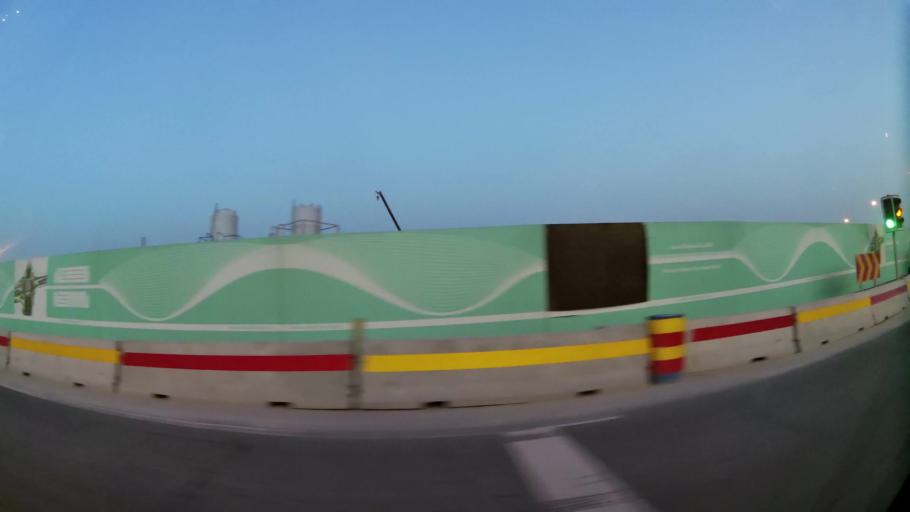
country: QA
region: Baladiyat ar Rayyan
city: Ar Rayyan
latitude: 25.3196
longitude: 51.4474
